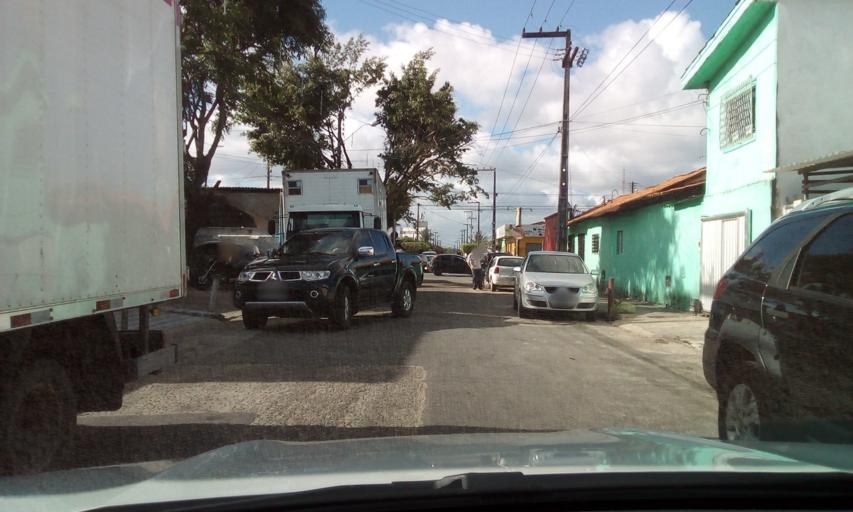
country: BR
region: Paraiba
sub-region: Joao Pessoa
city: Joao Pessoa
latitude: -7.1337
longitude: -34.8747
